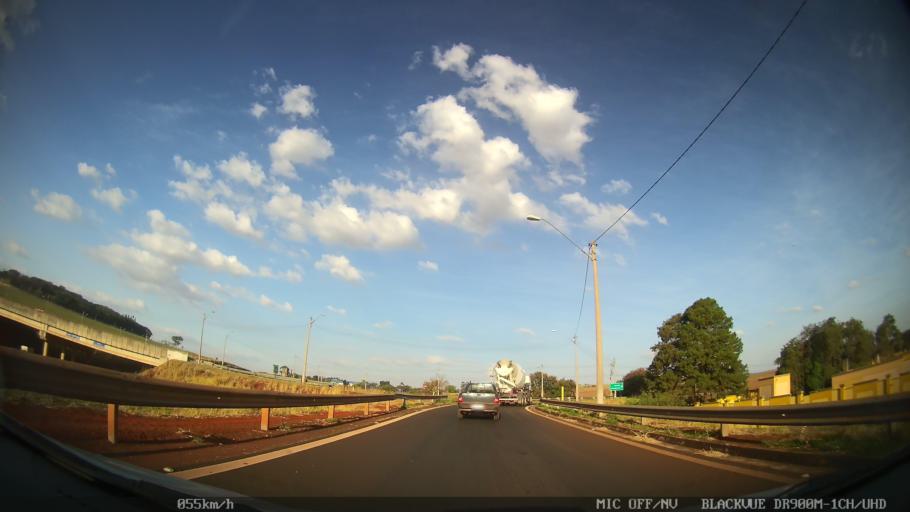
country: BR
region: Sao Paulo
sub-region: Ribeirao Preto
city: Ribeirao Preto
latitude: -21.2067
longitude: -47.7505
